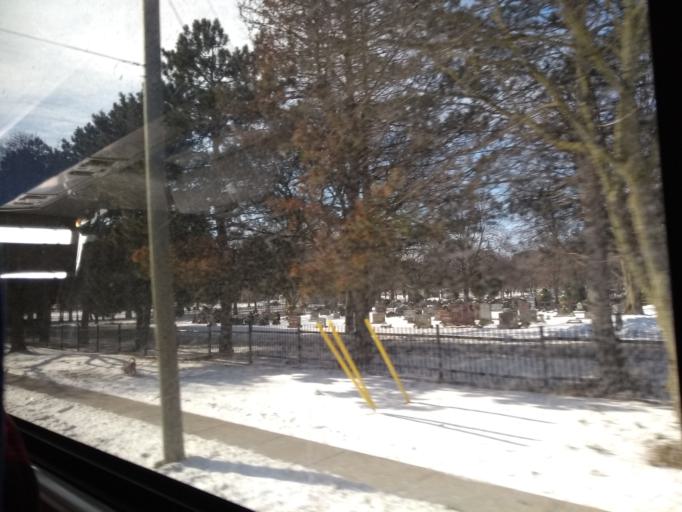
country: CA
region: Ontario
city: Niagara Falls
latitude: 43.1053
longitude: -79.0859
